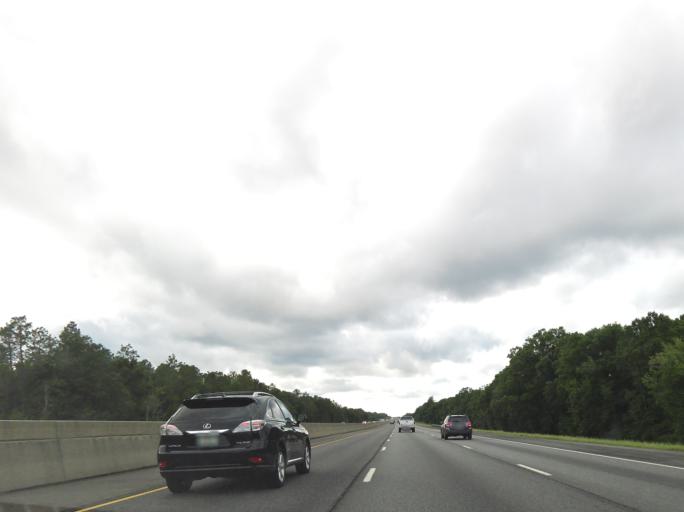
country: US
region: Georgia
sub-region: Turner County
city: Ashburn
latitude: 31.7706
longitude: -83.6783
